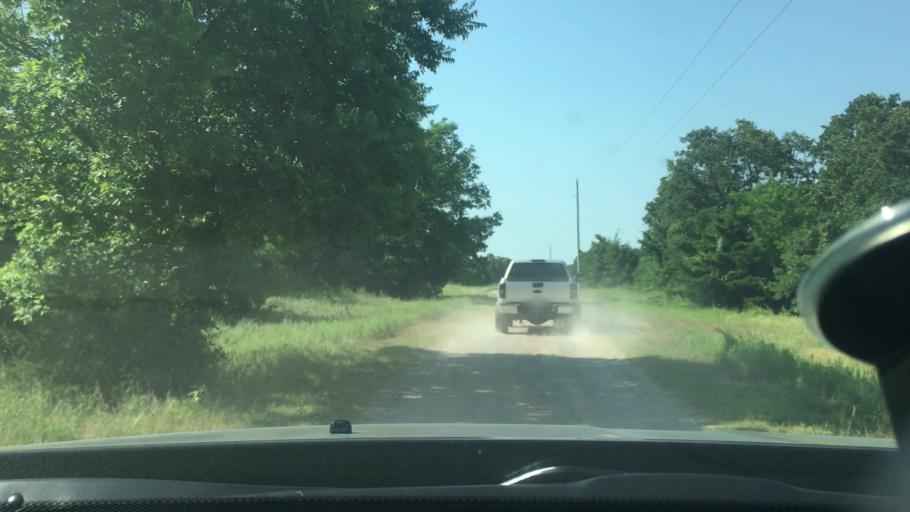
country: US
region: Oklahoma
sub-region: Garvin County
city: Lindsay
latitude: 34.7670
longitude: -97.6164
